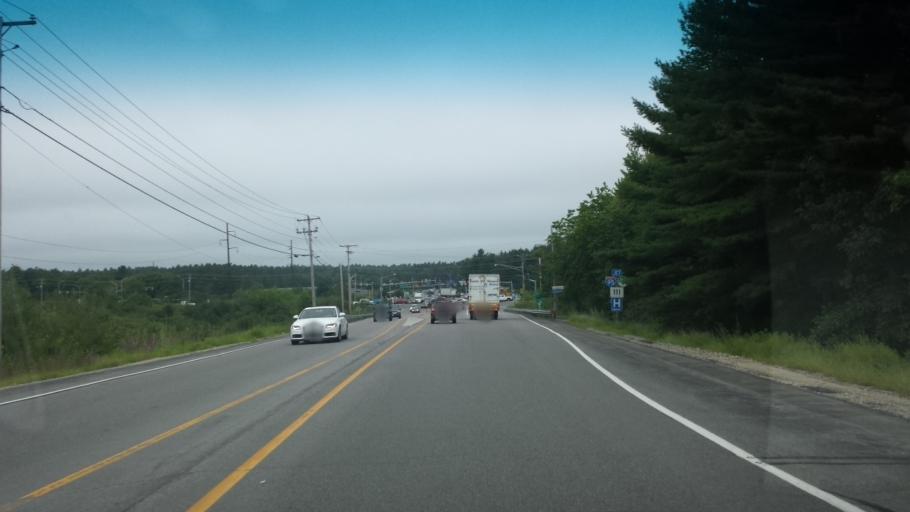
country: US
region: Maine
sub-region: York County
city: Biddeford
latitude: 43.4761
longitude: -70.4946
